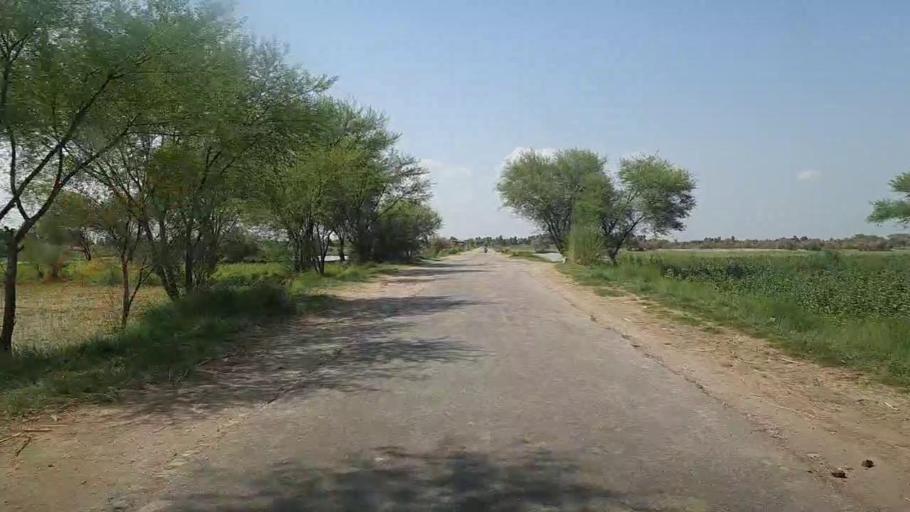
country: PK
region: Sindh
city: Khairpur
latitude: 28.0755
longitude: 69.6391
